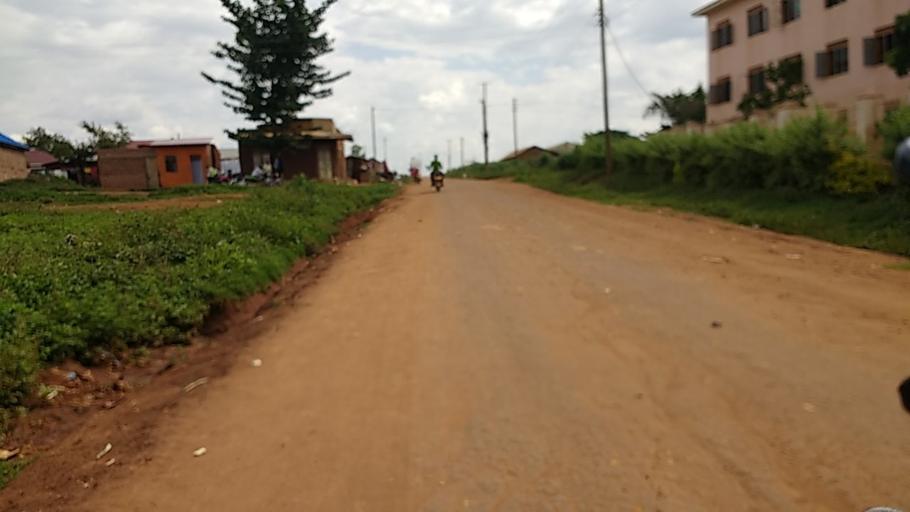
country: UG
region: Eastern Region
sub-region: Mbale District
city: Mbale
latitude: 1.0831
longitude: 34.1611
